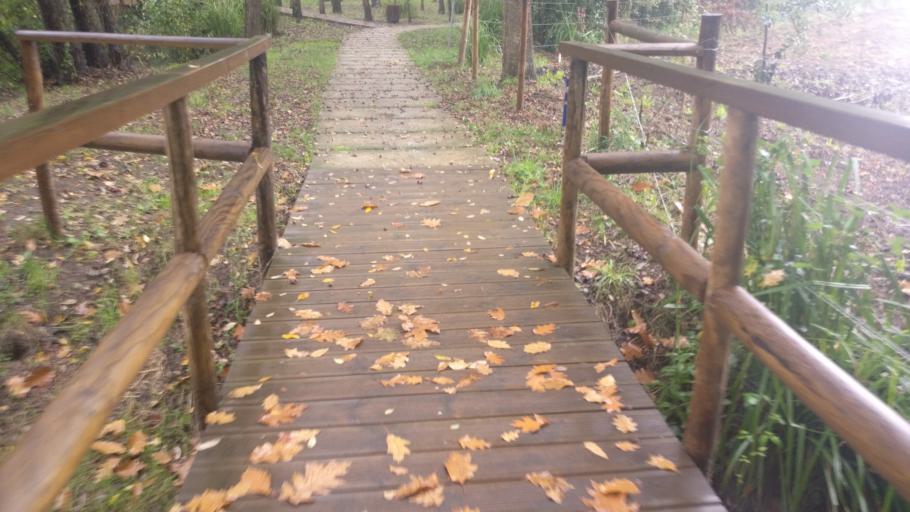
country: PT
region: Viseu
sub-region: Mortagua
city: Mortagua
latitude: 40.3944
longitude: -8.2267
